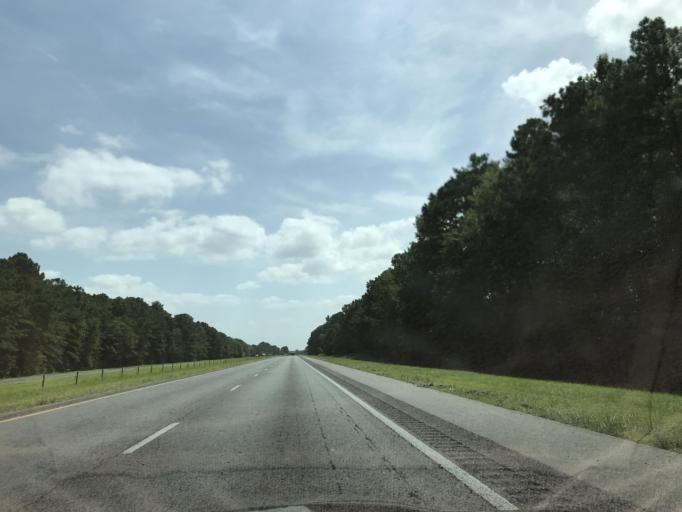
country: US
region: North Carolina
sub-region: Duplin County
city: Rose Hill
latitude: 34.8539
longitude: -77.9986
